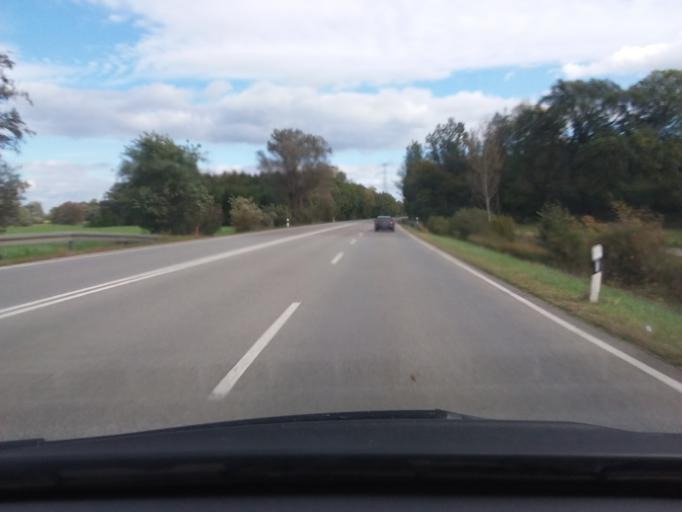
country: DE
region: Bavaria
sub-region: Upper Bavaria
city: Bergkirchen
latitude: 48.2394
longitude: 11.3850
